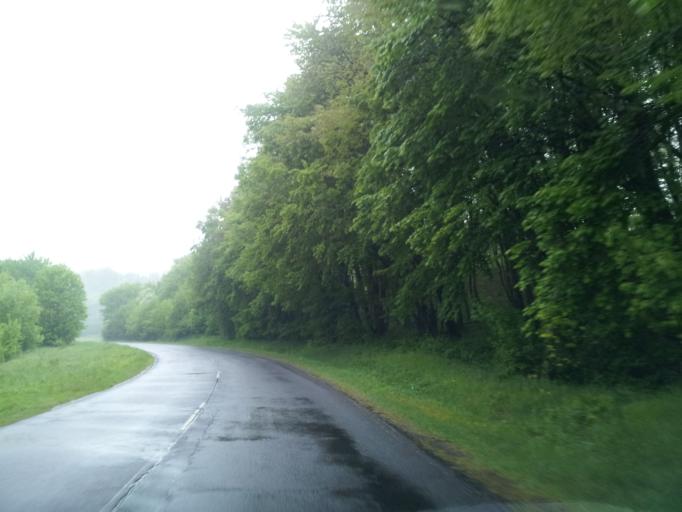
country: HU
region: Baranya
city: Hosszuheteny
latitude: 46.1949
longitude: 18.3143
